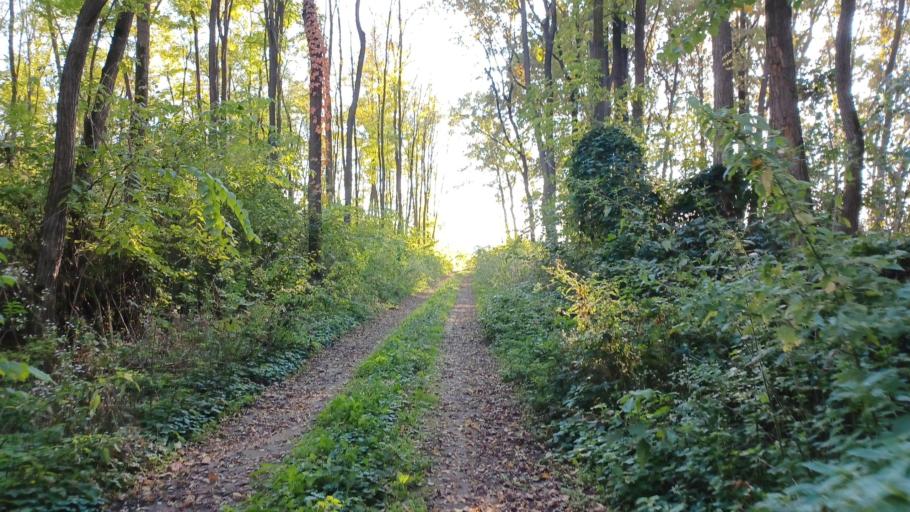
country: HU
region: Tolna
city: Tengelic
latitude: 46.5324
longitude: 18.7006
